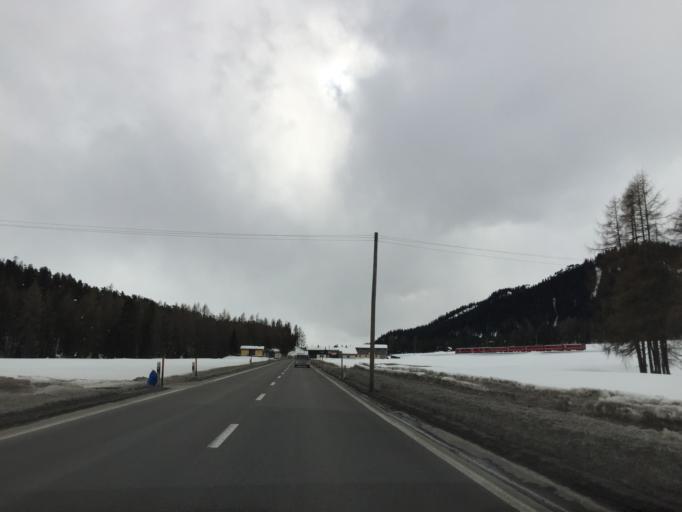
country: CH
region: Grisons
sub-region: Praettigau/Davos District
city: Davos
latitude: 46.8401
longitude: 9.8582
